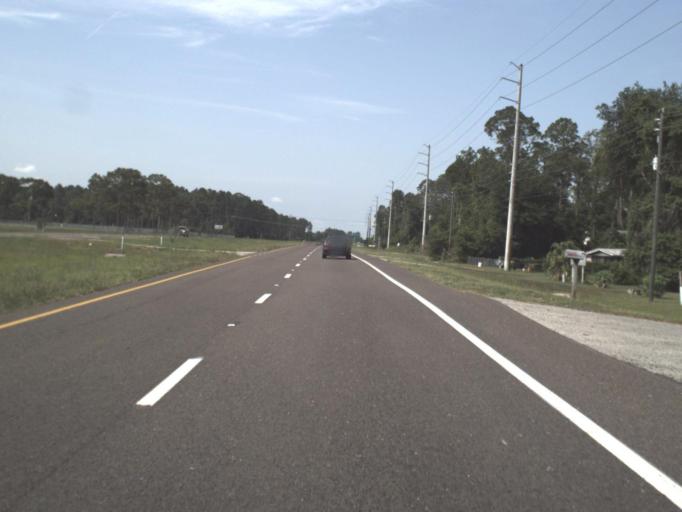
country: US
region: Florida
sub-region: Saint Johns County
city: Saint Augustine Shores
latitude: 29.7741
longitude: -81.4531
